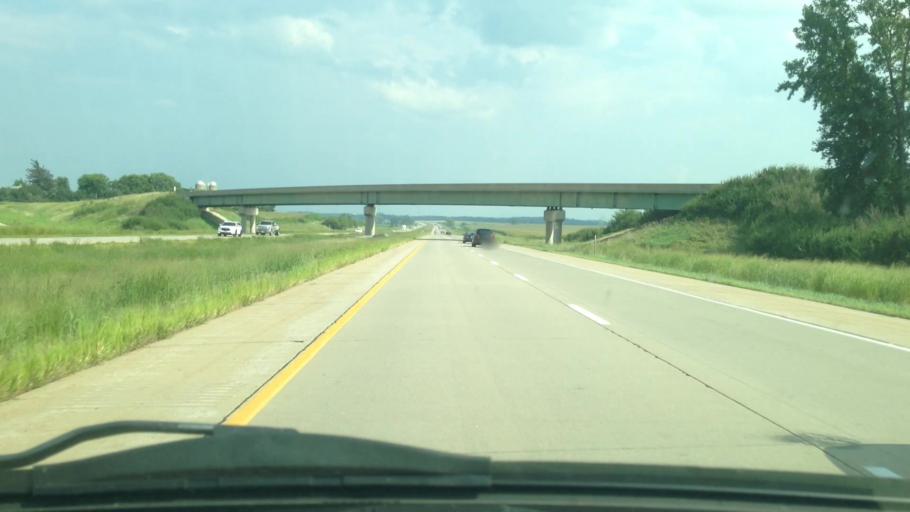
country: US
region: Iowa
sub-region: Black Hawk County
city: La Porte City
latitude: 42.3854
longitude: -92.1262
